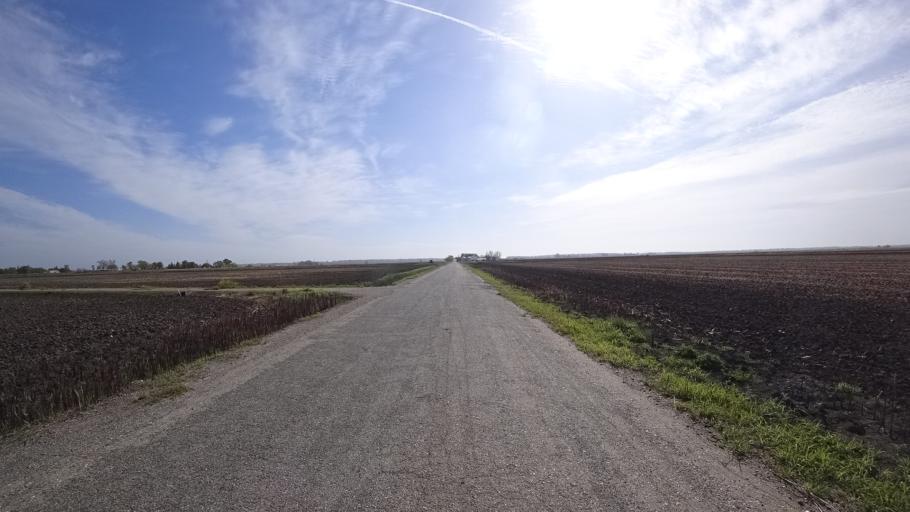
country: US
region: California
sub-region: Glenn County
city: Willows
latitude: 39.5726
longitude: -122.0444
